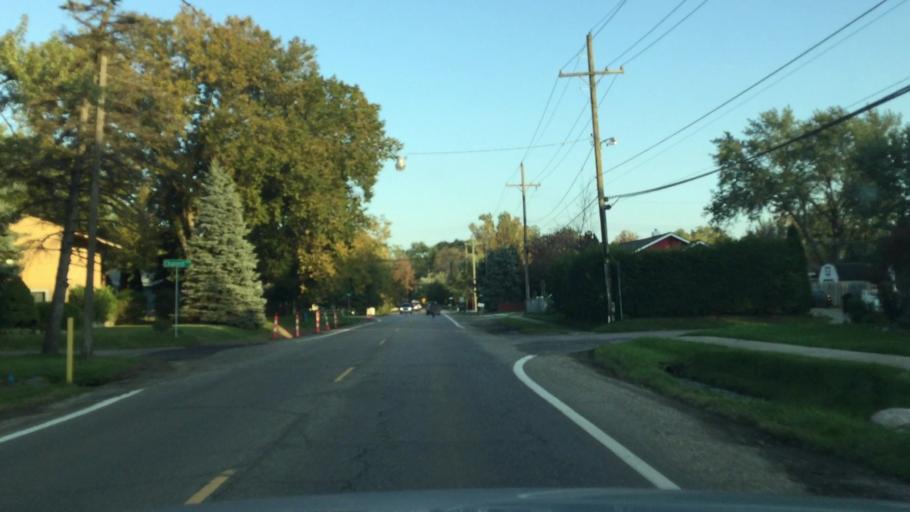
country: US
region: Michigan
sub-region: Oakland County
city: Keego Harbor
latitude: 42.6252
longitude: -83.3802
